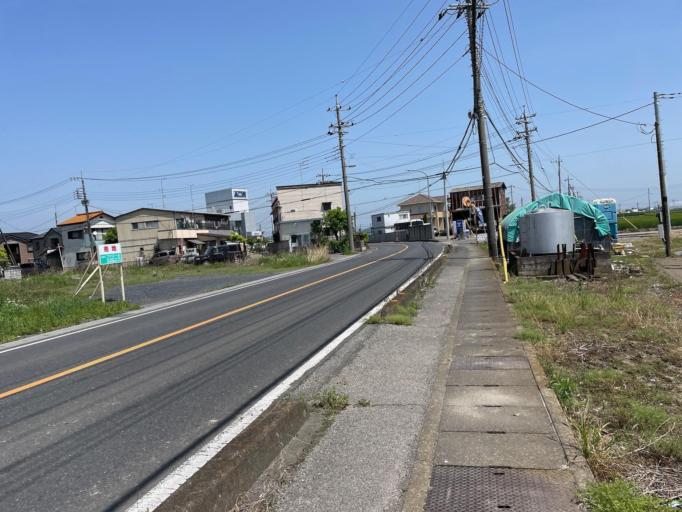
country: JP
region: Tochigi
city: Ashikaga
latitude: 36.3009
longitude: 139.4696
